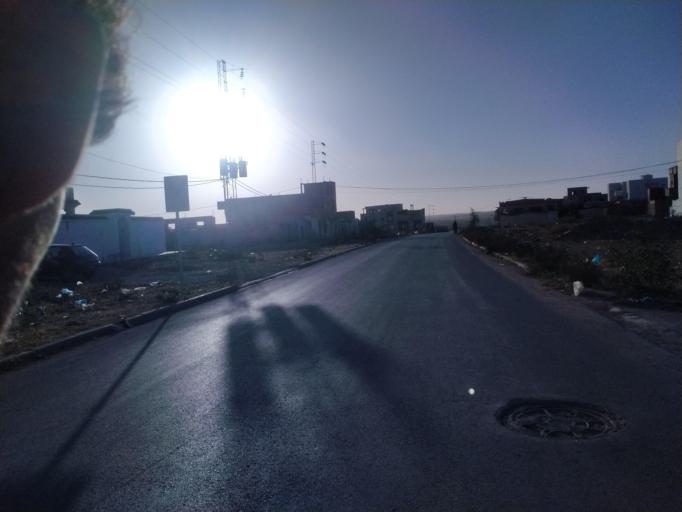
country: TN
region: Susah
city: Akouda
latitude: 35.8155
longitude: 10.5562
